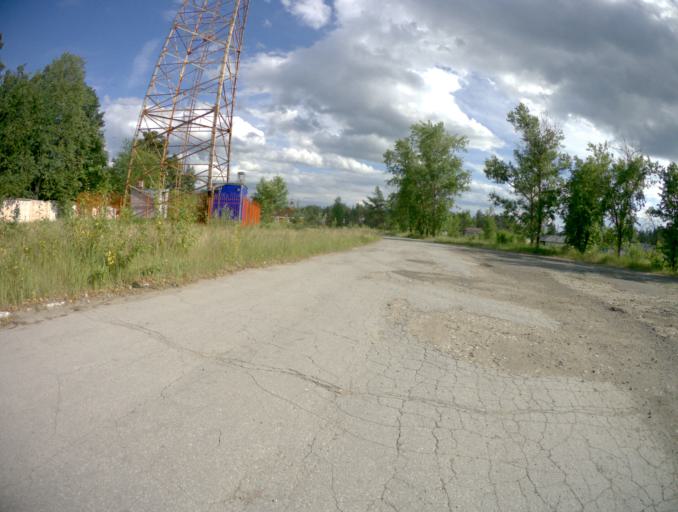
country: RU
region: Vladimir
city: Gorokhovets
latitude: 56.2954
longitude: 42.7852
